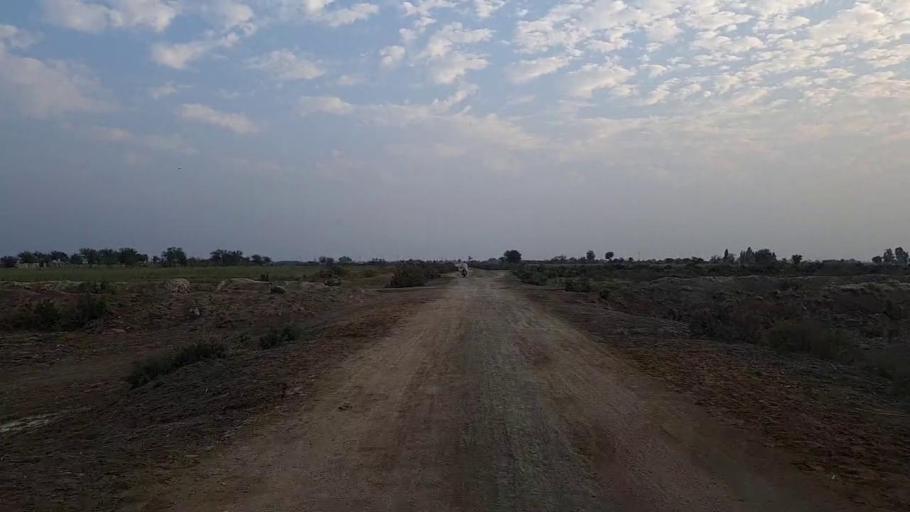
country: PK
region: Sindh
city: Pithoro
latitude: 25.4464
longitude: 69.3450
